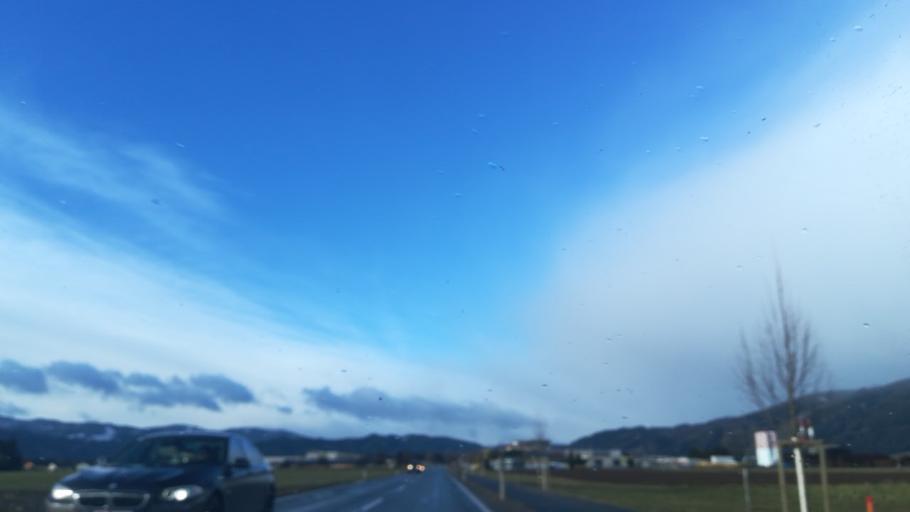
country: AT
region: Styria
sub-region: Politischer Bezirk Murtal
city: Zeltweg
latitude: 47.1947
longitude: 14.7390
